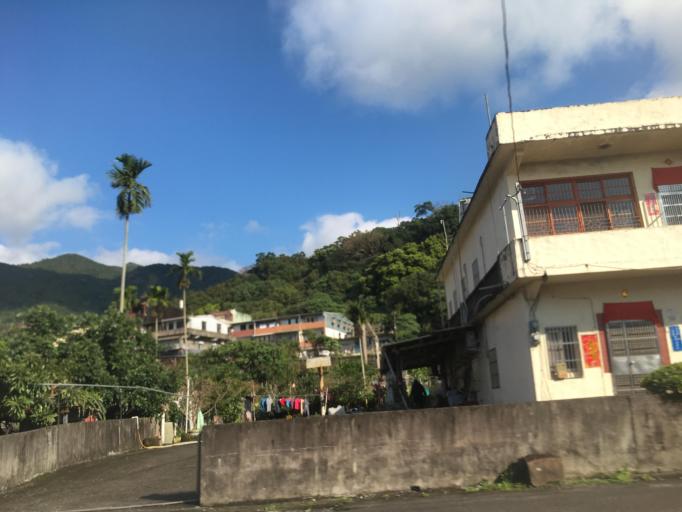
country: TW
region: Taiwan
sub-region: Yilan
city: Yilan
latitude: 24.9039
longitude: 121.8669
